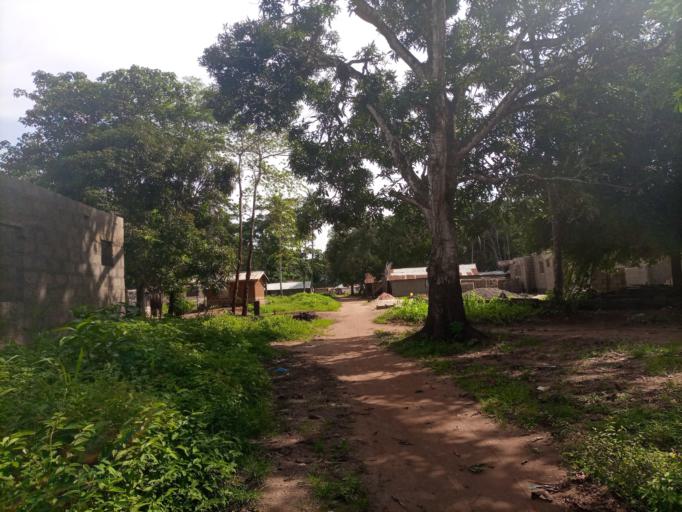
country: SL
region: Northern Province
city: Sawkta
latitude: 8.6313
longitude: -13.1830
